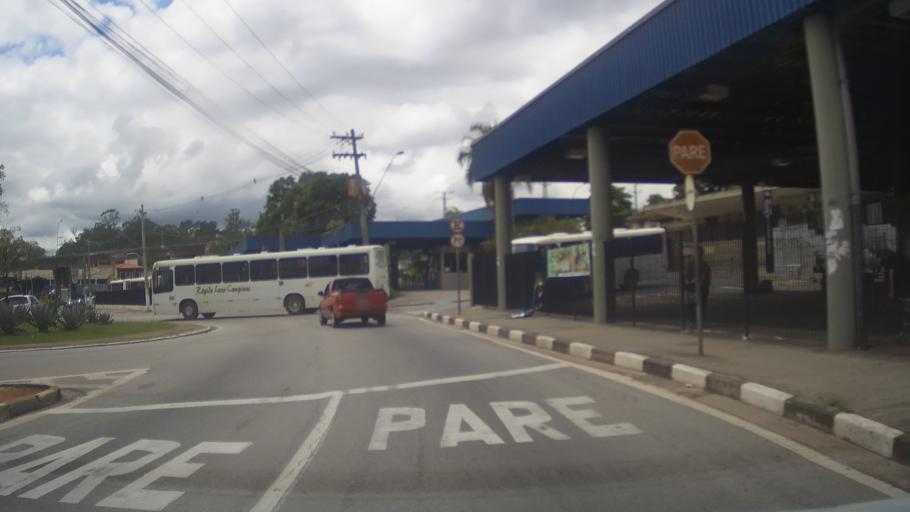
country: BR
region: Sao Paulo
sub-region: Campo Limpo Paulista
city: Campo Limpo Paulista
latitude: -23.2062
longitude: -46.7855
